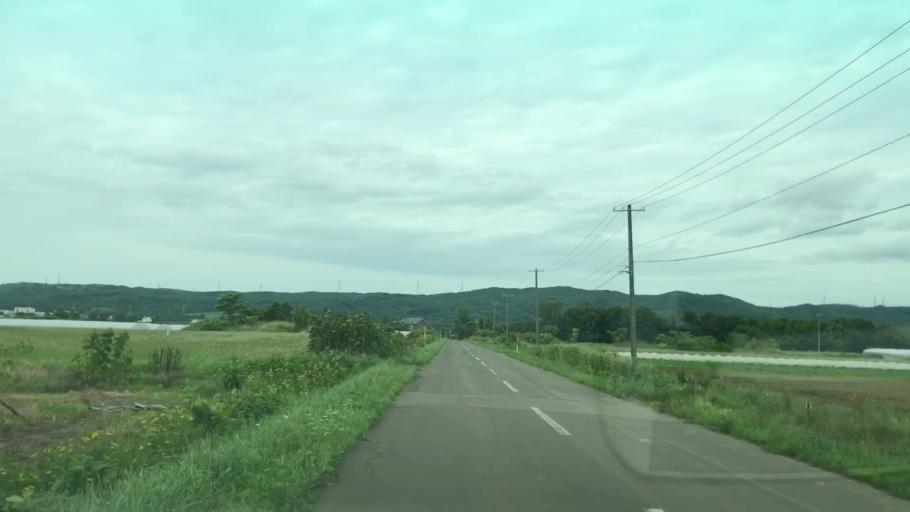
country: JP
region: Hokkaido
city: Iwanai
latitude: 43.0314
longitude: 140.5701
